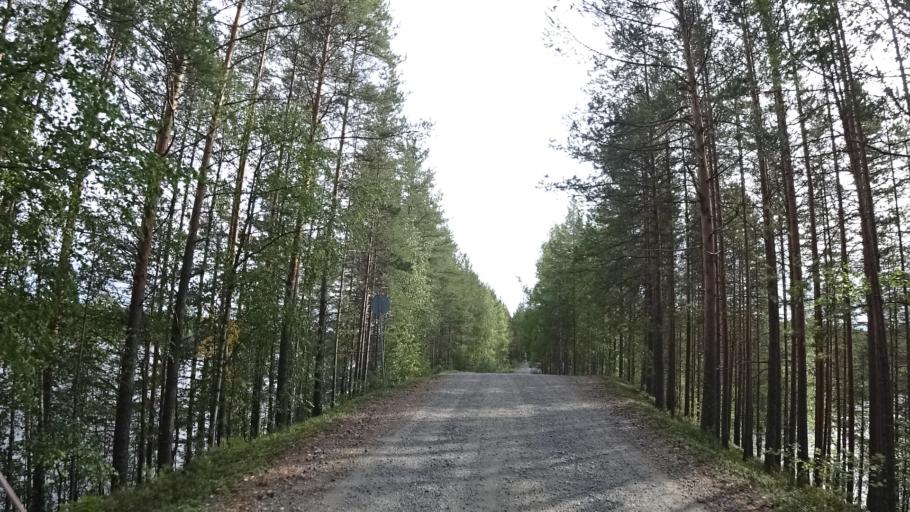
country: FI
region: North Karelia
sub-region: Joensuu
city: Ilomantsi
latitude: 62.6159
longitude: 31.1962
